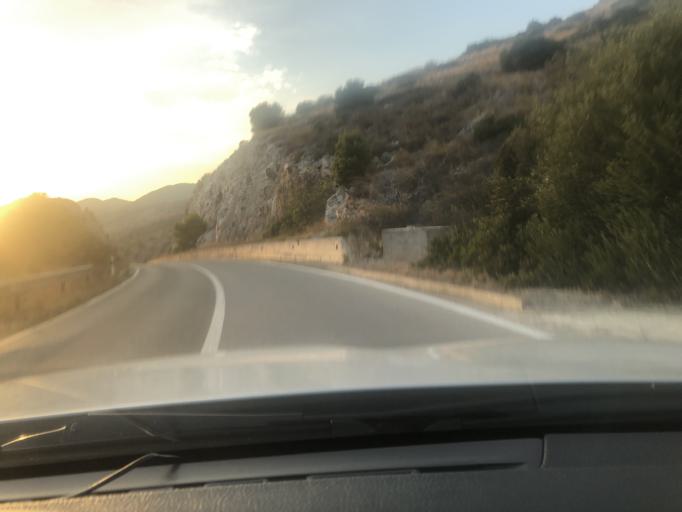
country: HR
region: Splitsko-Dalmatinska
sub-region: Grad Hvar
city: Hvar
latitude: 43.1553
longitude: 16.5099
